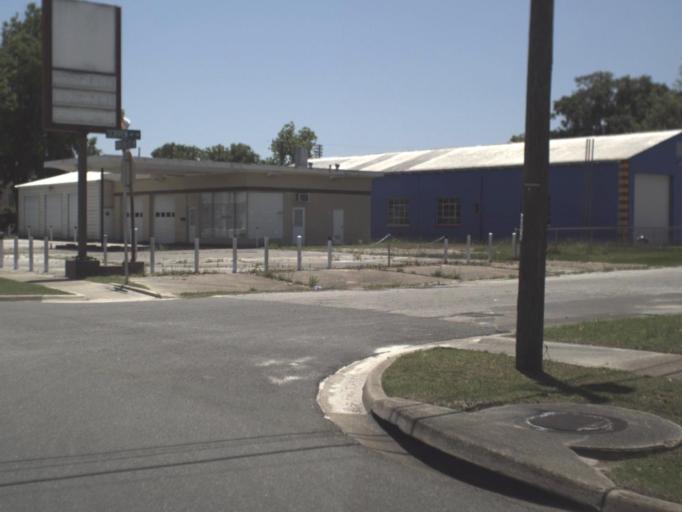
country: US
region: Florida
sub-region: Suwannee County
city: Live Oak
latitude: 30.2985
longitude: -82.9899
